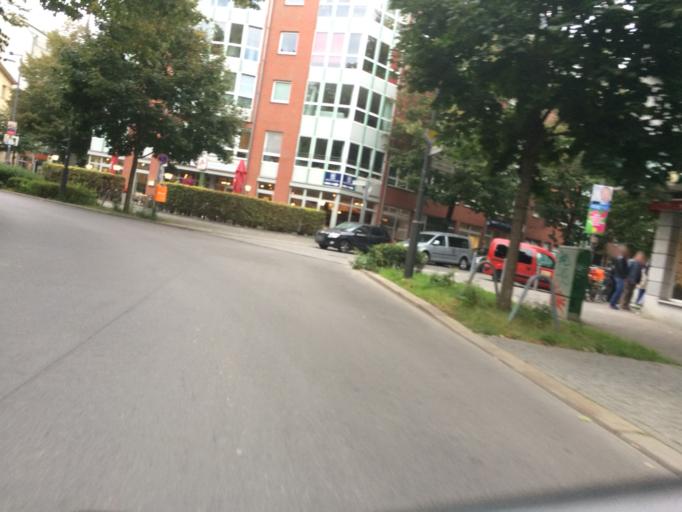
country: DE
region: Berlin
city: Weissensee
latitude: 52.5531
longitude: 13.4491
